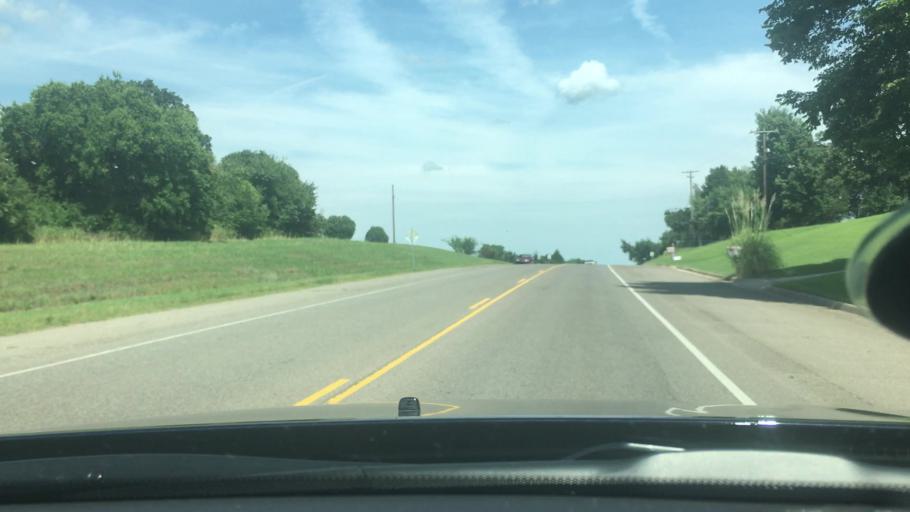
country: US
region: Oklahoma
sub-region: Pottawatomie County
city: Shawnee
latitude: 35.3331
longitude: -96.8667
